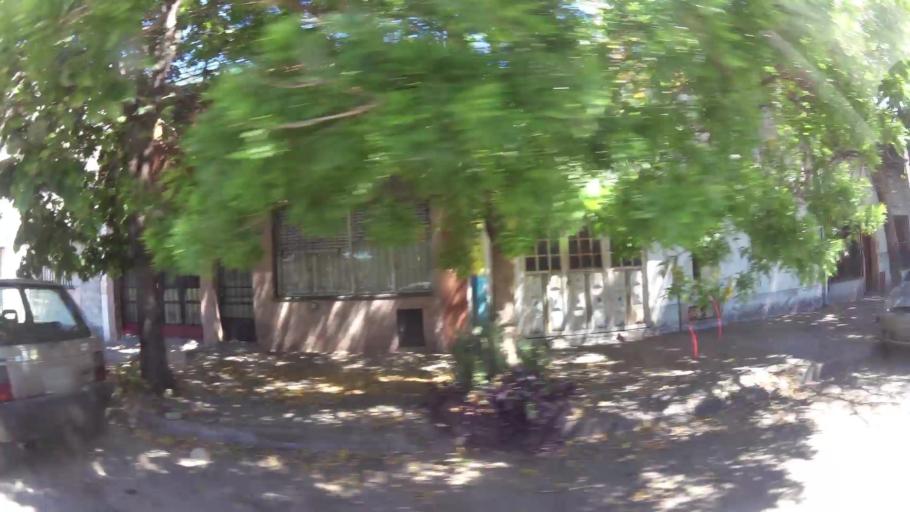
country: AR
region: Santa Fe
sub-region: Departamento de Rosario
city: Rosario
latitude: -32.9335
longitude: -60.6745
